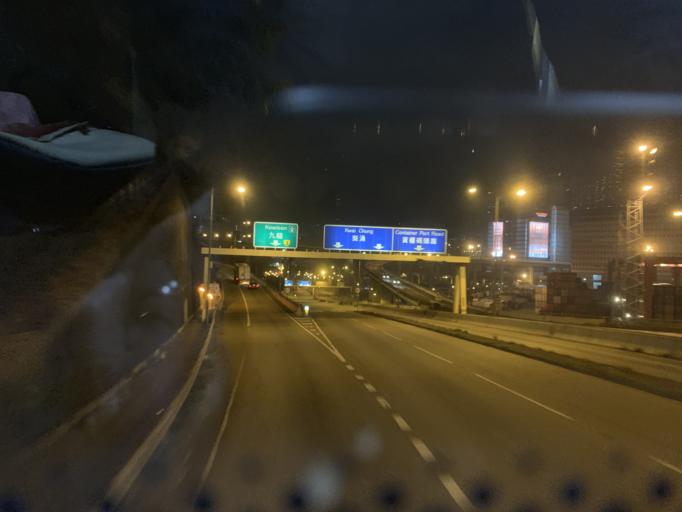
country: HK
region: Tsuen Wan
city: Tsuen Wan
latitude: 22.3501
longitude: 114.1179
